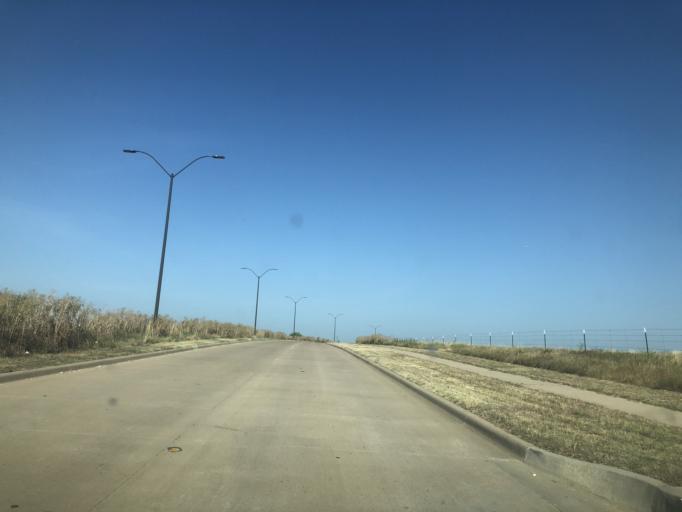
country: US
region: Texas
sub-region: Tarrant County
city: Crowley
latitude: 32.6065
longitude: -97.4161
